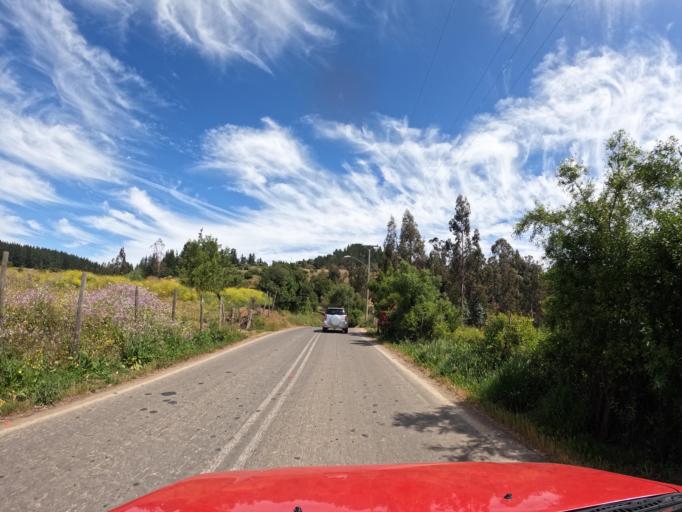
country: CL
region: Maule
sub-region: Provincia de Talca
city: Constitucion
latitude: -34.9939
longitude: -72.0076
